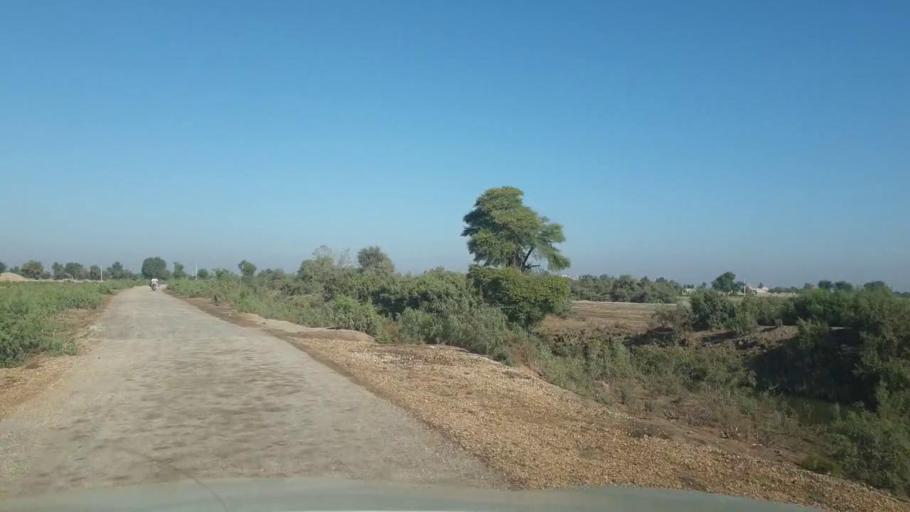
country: PK
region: Sindh
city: Bhan
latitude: 26.5373
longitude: 67.6588
